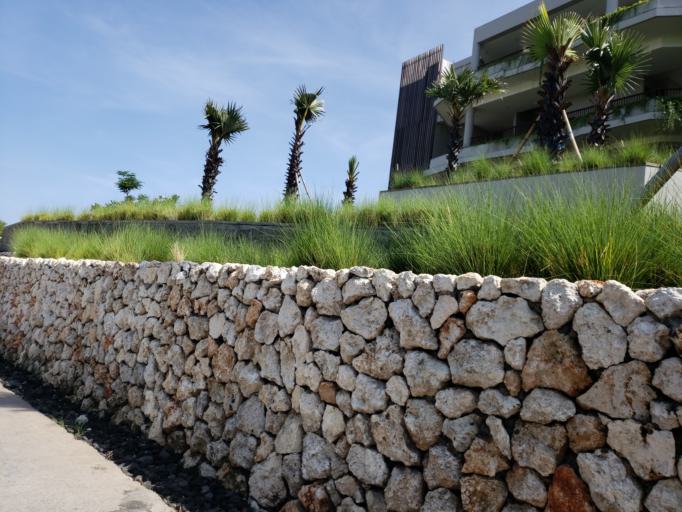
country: ID
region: Bali
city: Kangin
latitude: -8.8441
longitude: 115.1310
